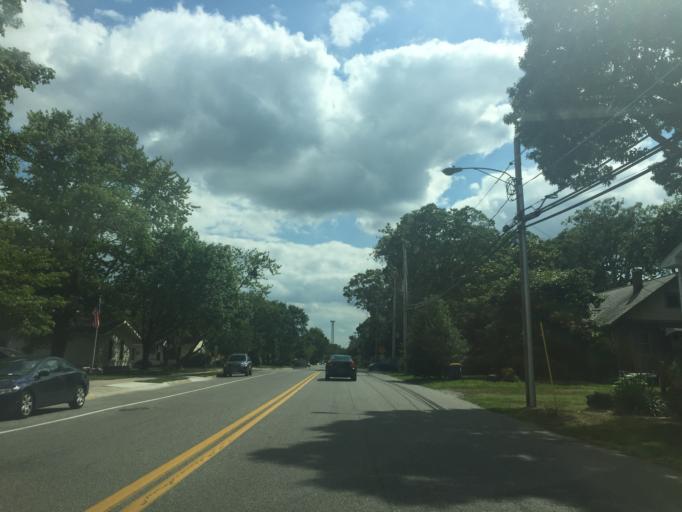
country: US
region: Delaware
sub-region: Sussex County
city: Rehoboth Beach
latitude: 38.7144
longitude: -75.0893
